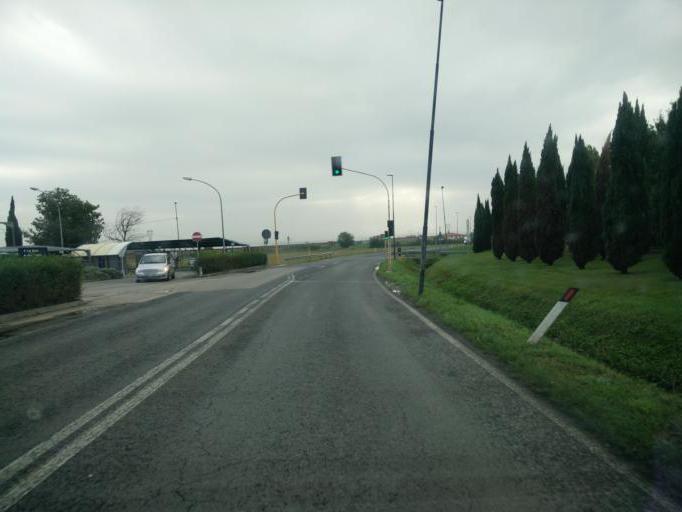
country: IT
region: Tuscany
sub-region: Province of Florence
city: Campi Bisenzio
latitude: 43.8237
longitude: 11.1463
